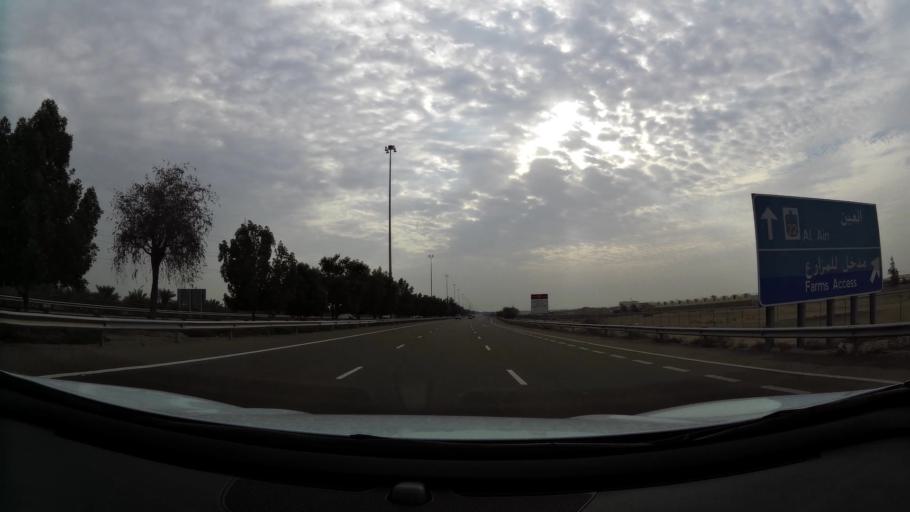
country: AE
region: Abu Dhabi
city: Abu Dhabi
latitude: 24.1898
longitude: 55.0122
